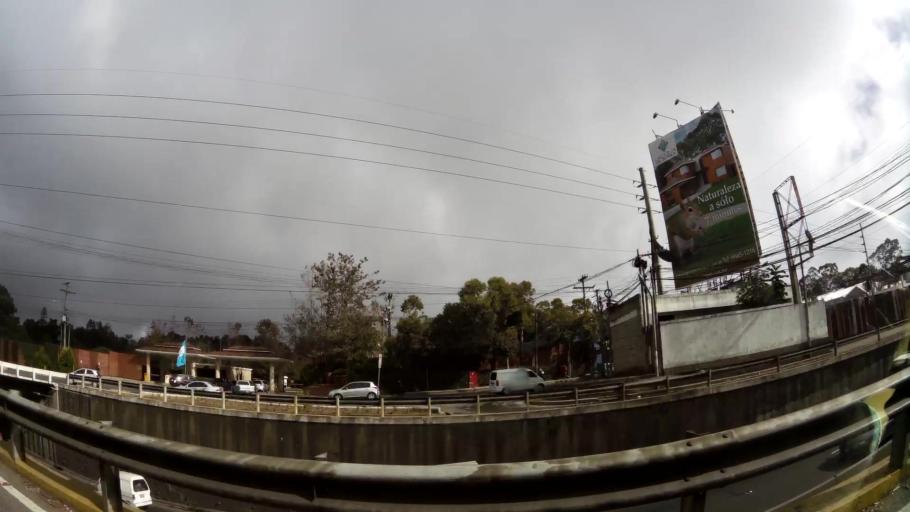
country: GT
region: Guatemala
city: Santa Catarina Pinula
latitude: 14.5650
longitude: -90.4672
